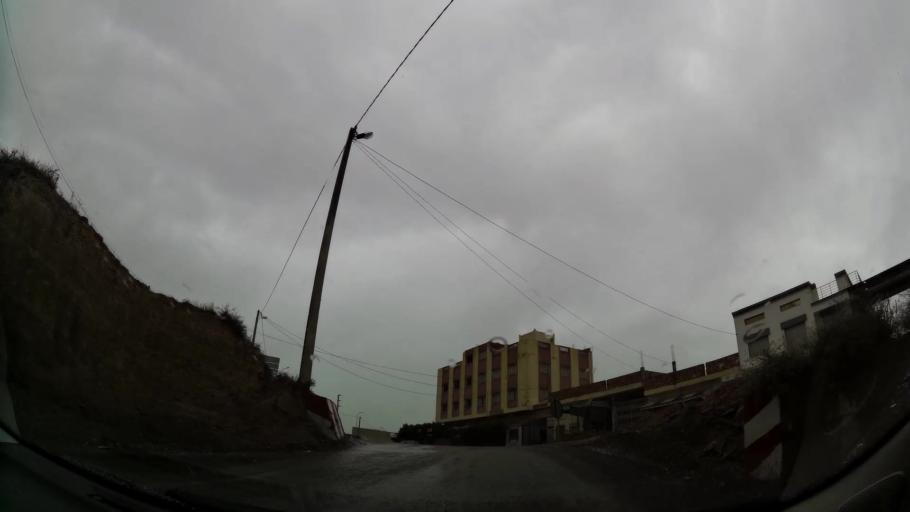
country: MA
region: Oriental
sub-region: Nador
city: Midar
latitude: 34.8908
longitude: -3.7336
